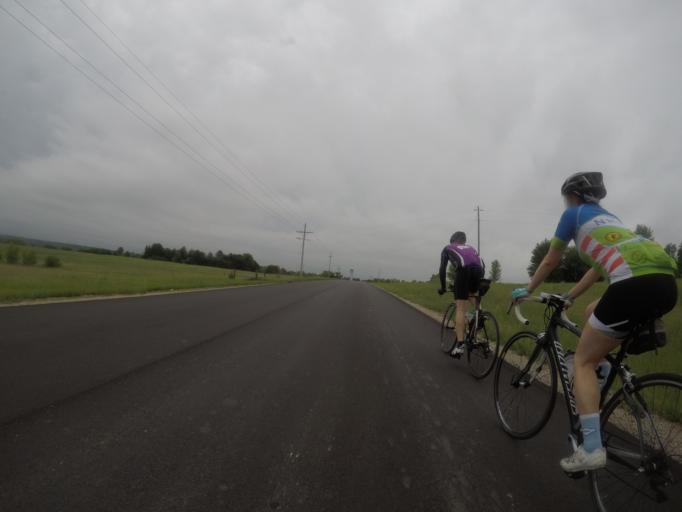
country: US
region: Kansas
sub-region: Pottawatomie County
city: Westmoreland
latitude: 39.5070
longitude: -96.1697
